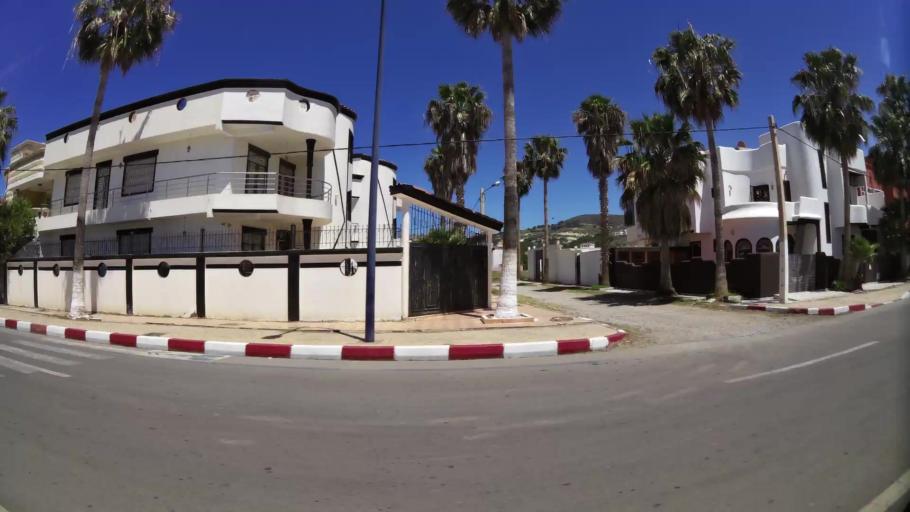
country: MA
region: Oriental
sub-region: Berkane-Taourirt
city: Madagh
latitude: 35.0726
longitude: -2.2182
